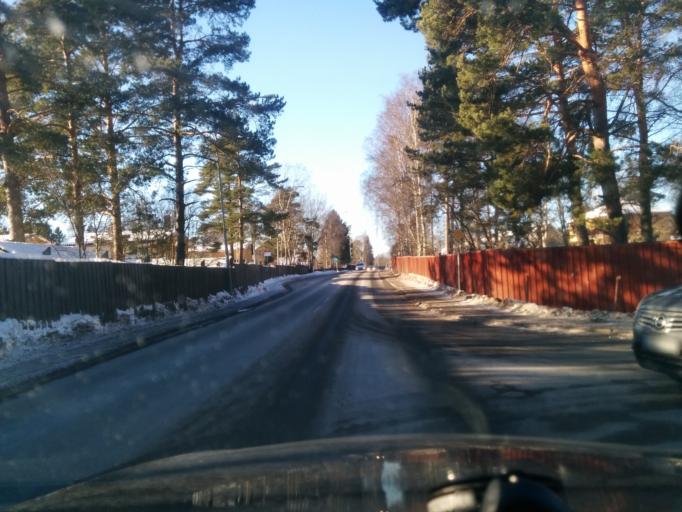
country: SE
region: Stockholm
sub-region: Vallentuna Kommun
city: Vallentuna
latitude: 59.4976
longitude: 18.0702
